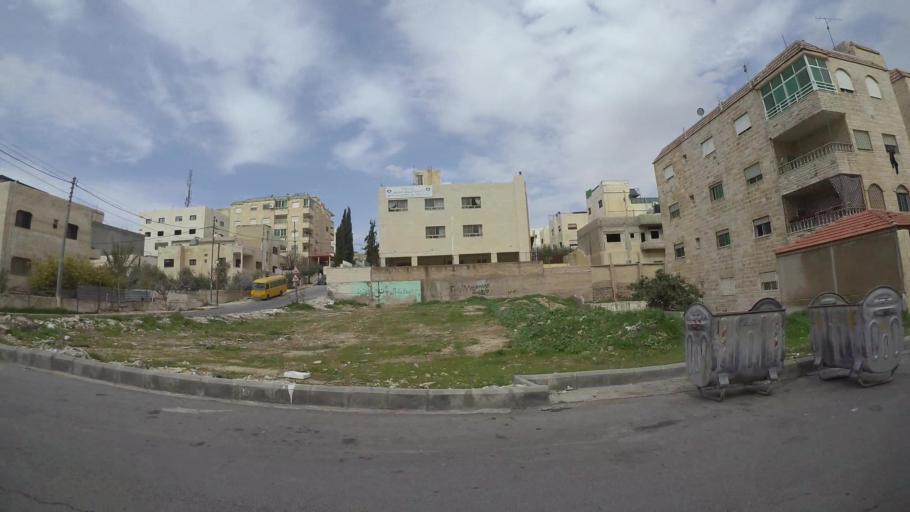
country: JO
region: Amman
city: Amman
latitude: 31.9954
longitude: 35.9410
